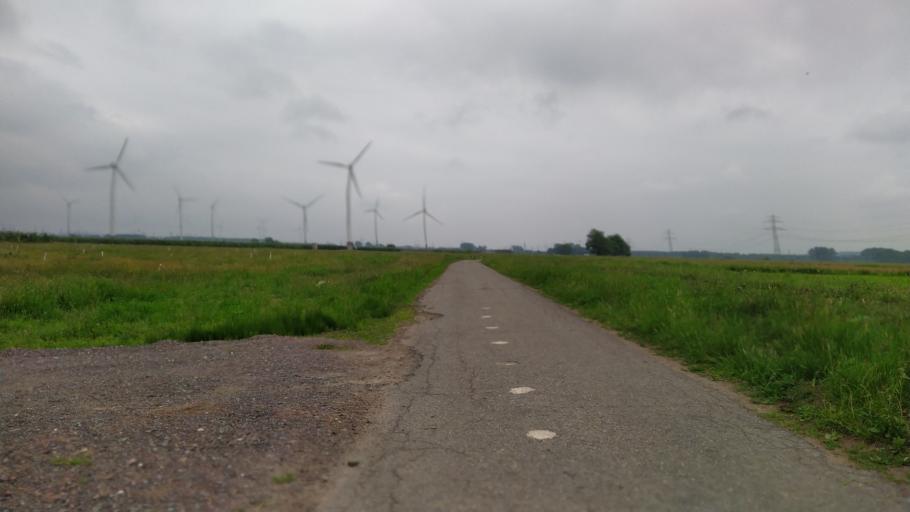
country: DE
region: Lower Saxony
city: Neu Wulmstorf
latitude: 53.4960
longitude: 9.8315
